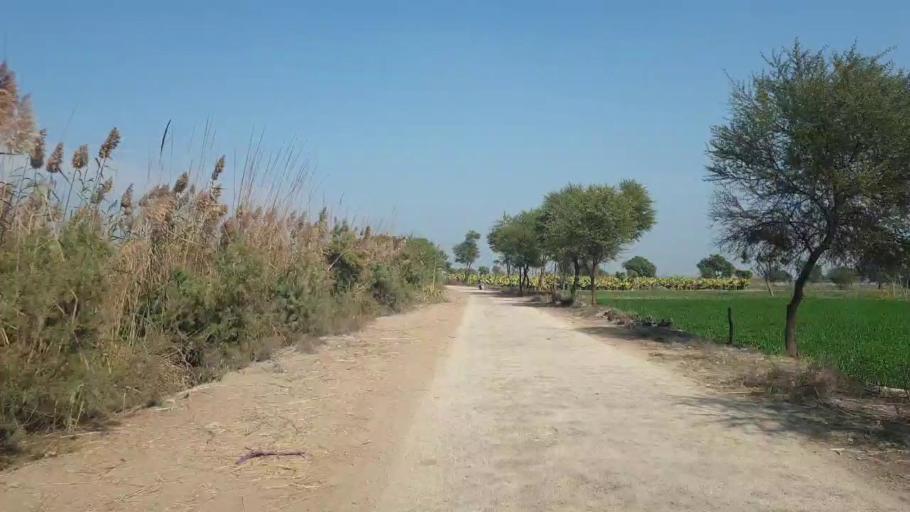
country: PK
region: Sindh
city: Shahdadpur
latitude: 25.9749
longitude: 68.5286
